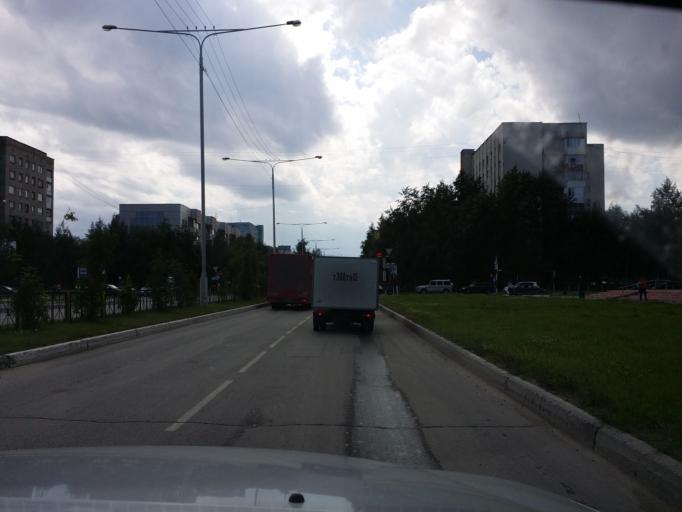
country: RU
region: Khanty-Mansiyskiy Avtonomnyy Okrug
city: Nizhnevartovsk
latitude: 60.9462
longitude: 76.5660
